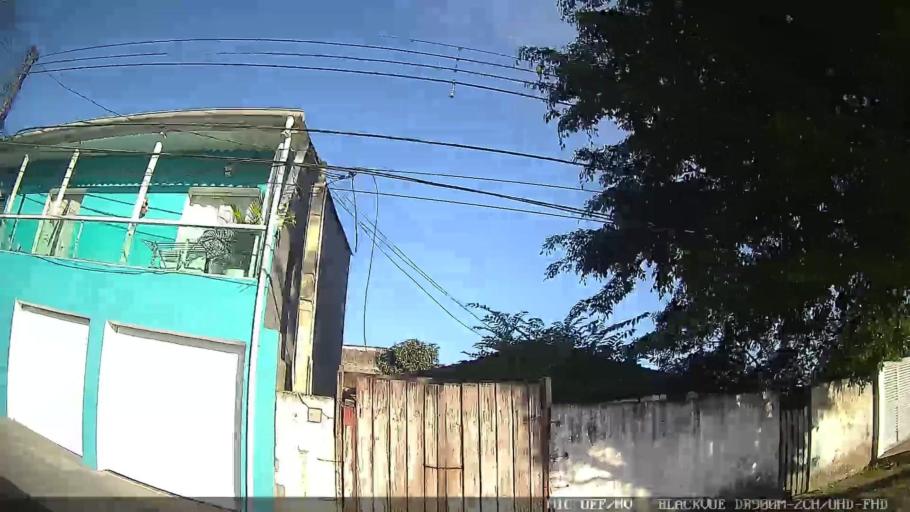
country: BR
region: Sao Paulo
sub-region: Guaruja
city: Guaruja
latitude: -23.9625
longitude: -46.2798
